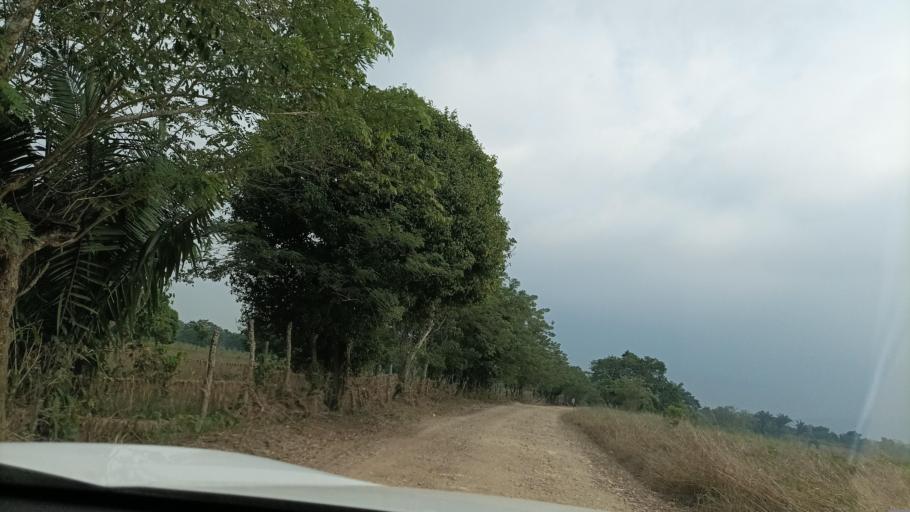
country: MX
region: Veracruz
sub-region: Moloacan
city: Cuichapa
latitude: 17.5836
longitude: -94.2157
